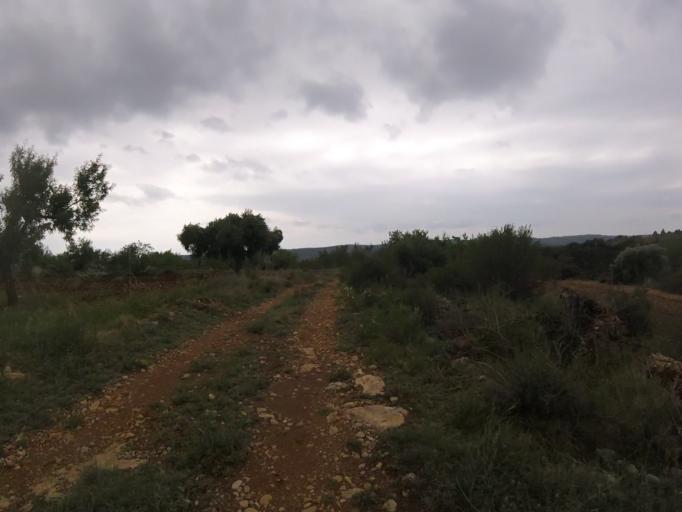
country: ES
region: Valencia
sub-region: Provincia de Castello
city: Cuevas de Vinroma
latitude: 40.2925
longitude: 0.0886
